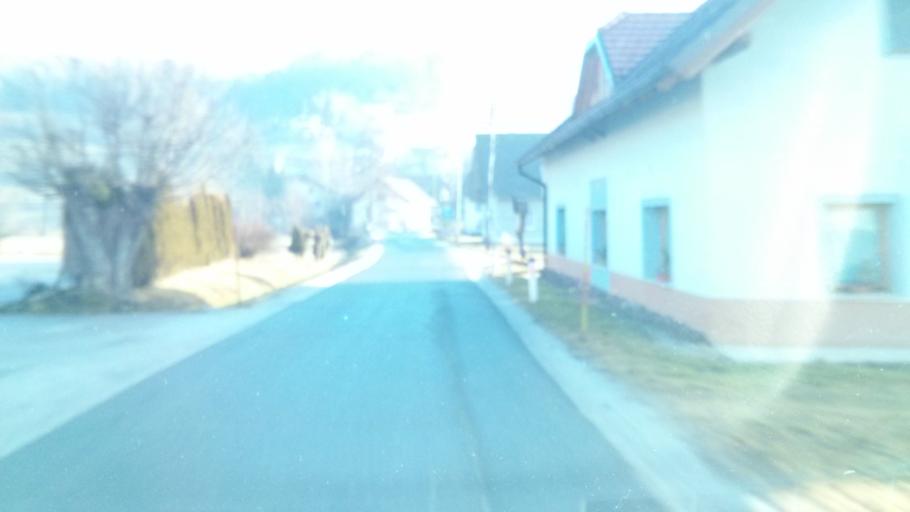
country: SI
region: Trebnje
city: Mirna
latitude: 45.9980
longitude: 14.9679
